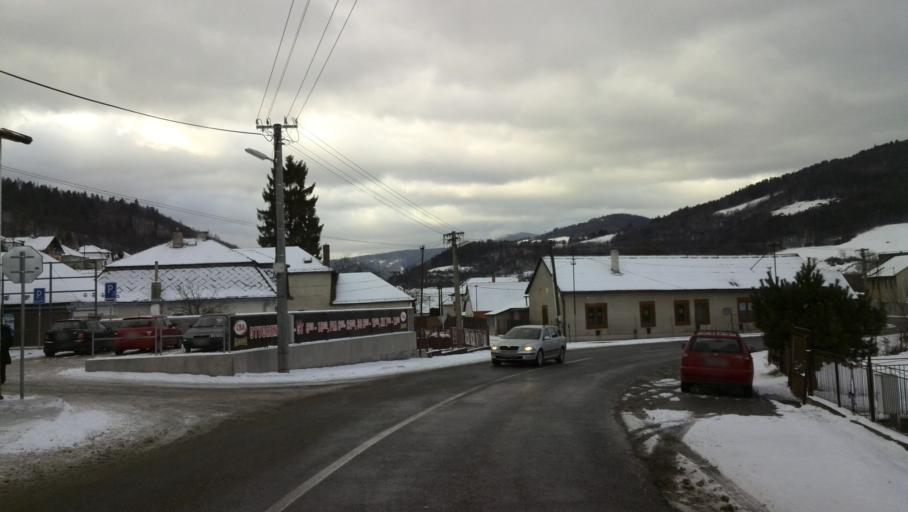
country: SK
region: Kosicky
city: Gelnica
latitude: 48.8735
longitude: 20.9918
